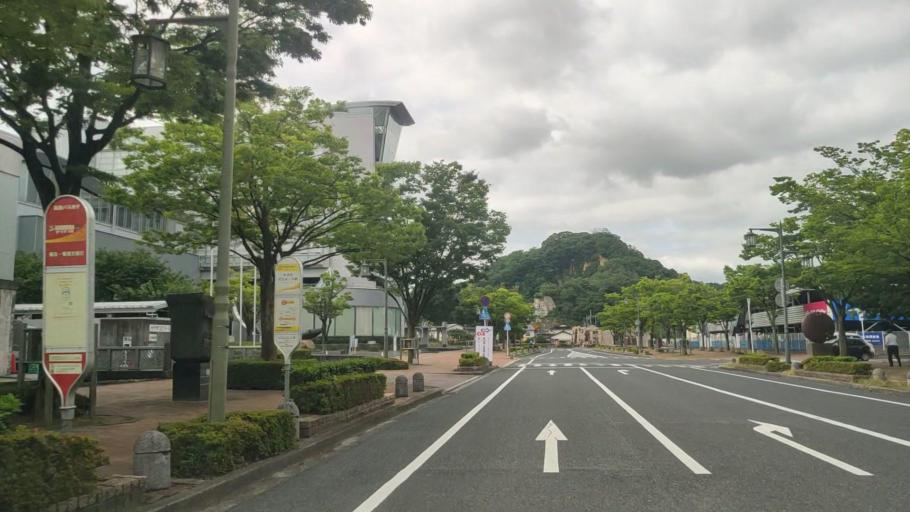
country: JP
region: Tottori
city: Yonago
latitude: 35.4224
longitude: 133.3334
